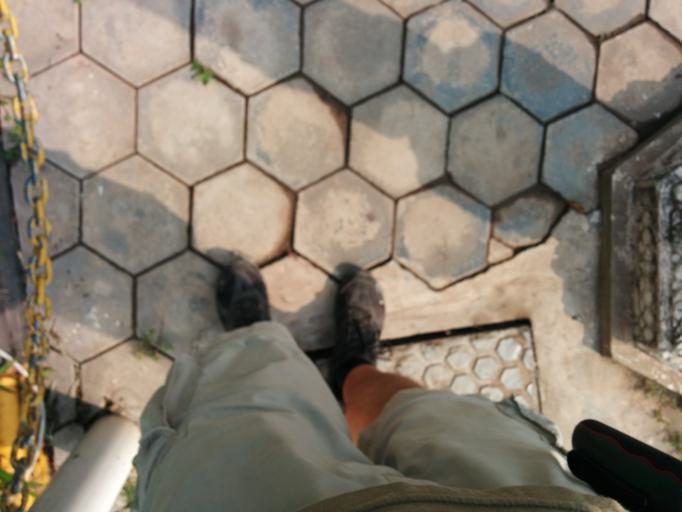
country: KH
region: Siem Reap
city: Siem Reap
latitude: 13.3573
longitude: 103.8581
